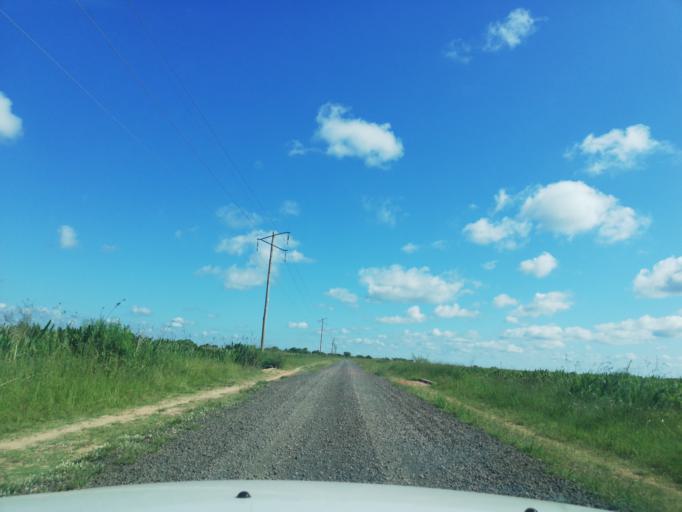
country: AR
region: Corrientes
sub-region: Departamento de San Miguel
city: San Miguel
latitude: -27.9769
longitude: -57.5808
